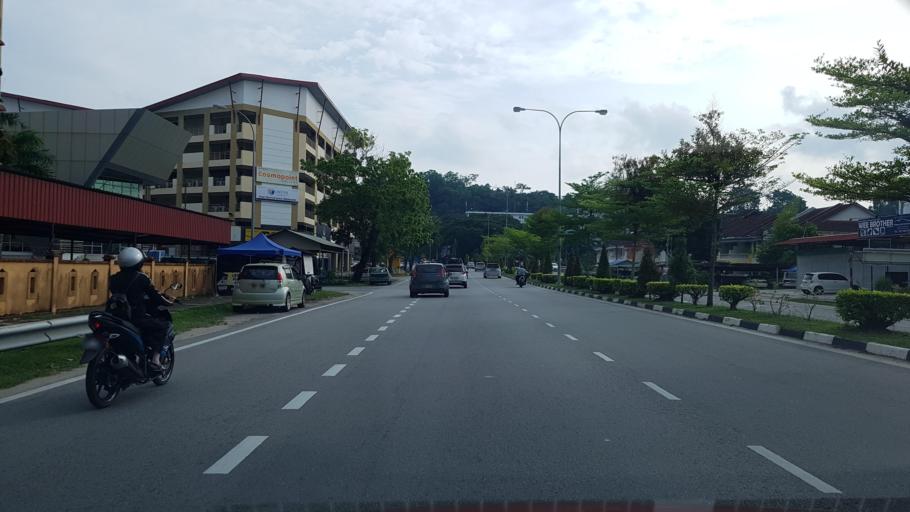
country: MY
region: Terengganu
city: Kuala Terengganu
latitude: 5.3261
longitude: 103.1381
